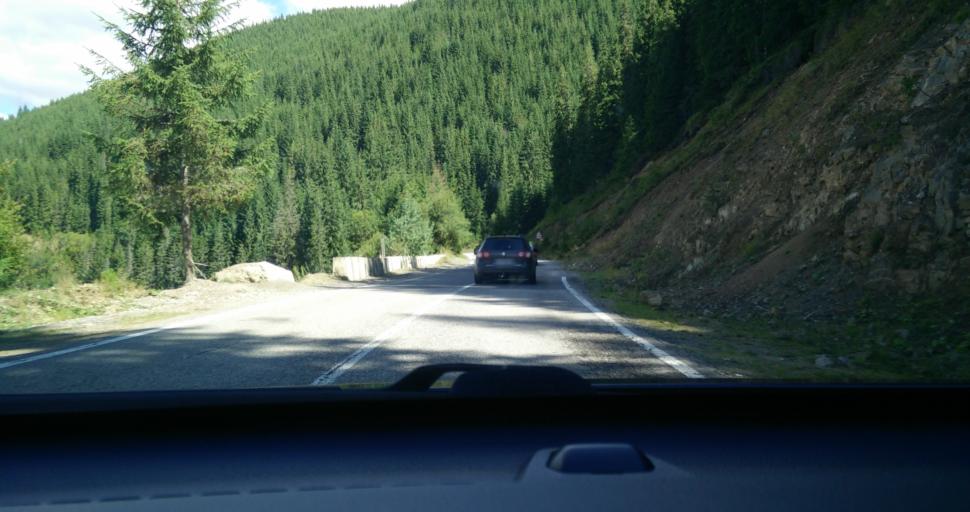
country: RO
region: Alba
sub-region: Comuna Sugag
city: Sugag
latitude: 45.5430
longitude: 23.6375
